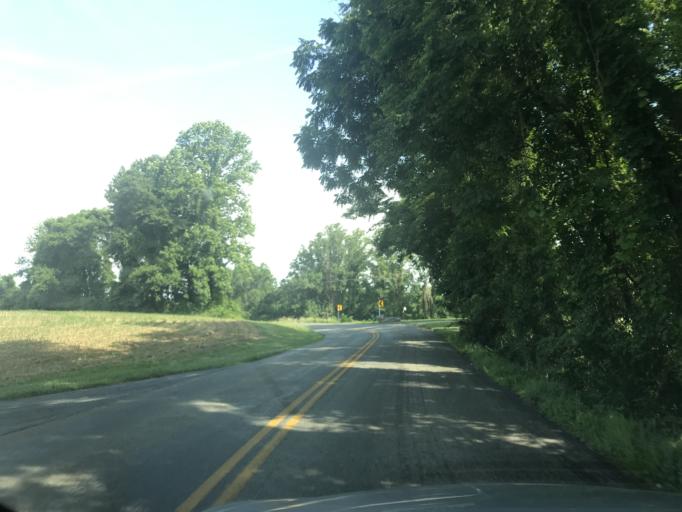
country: US
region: Maryland
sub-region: Harford County
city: Bel Air North
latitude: 39.5585
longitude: -76.4149
